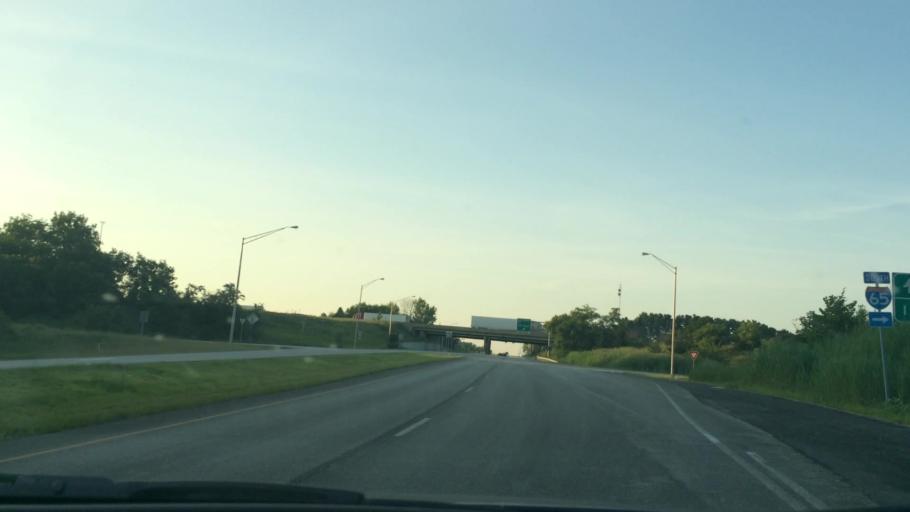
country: US
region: Indiana
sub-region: Tippecanoe County
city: Battle Ground
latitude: 40.4946
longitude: -86.8683
